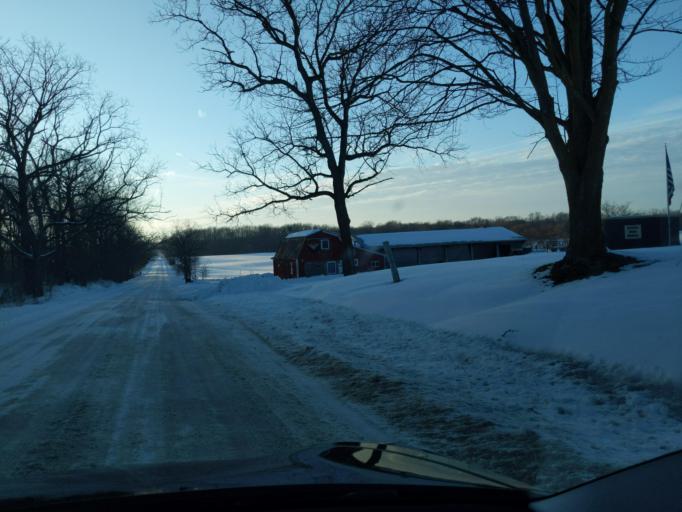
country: US
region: Michigan
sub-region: Livingston County
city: Fowlerville
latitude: 42.5680
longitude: -84.1186
